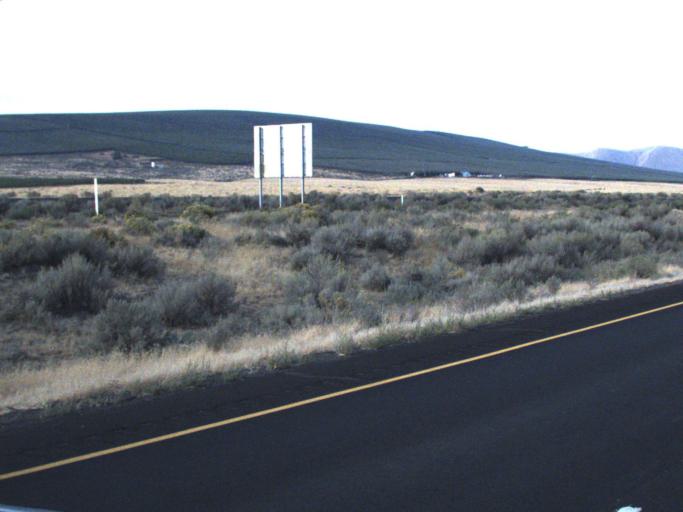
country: US
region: Washington
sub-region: Benton County
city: West Richland
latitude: 46.2621
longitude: -119.4065
